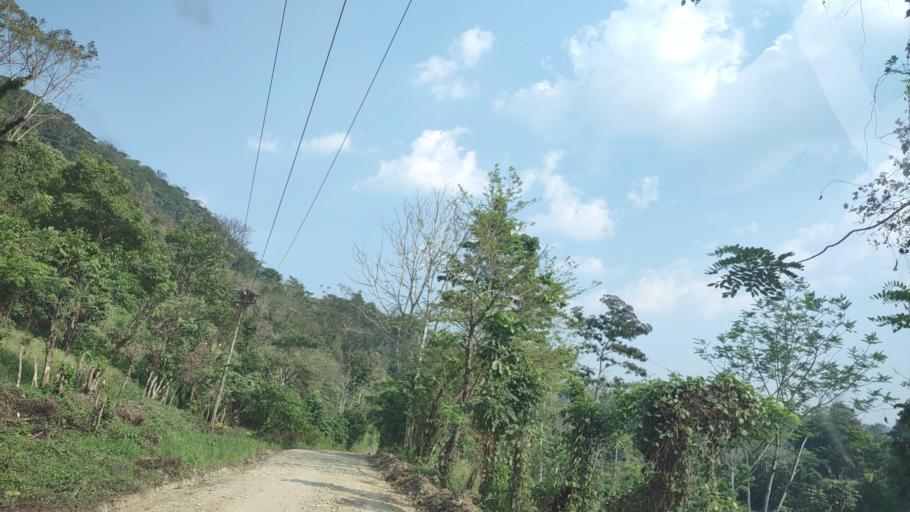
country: MX
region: Chiapas
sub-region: Tecpatan
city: Raudales Malpaso
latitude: 17.3210
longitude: -93.7423
